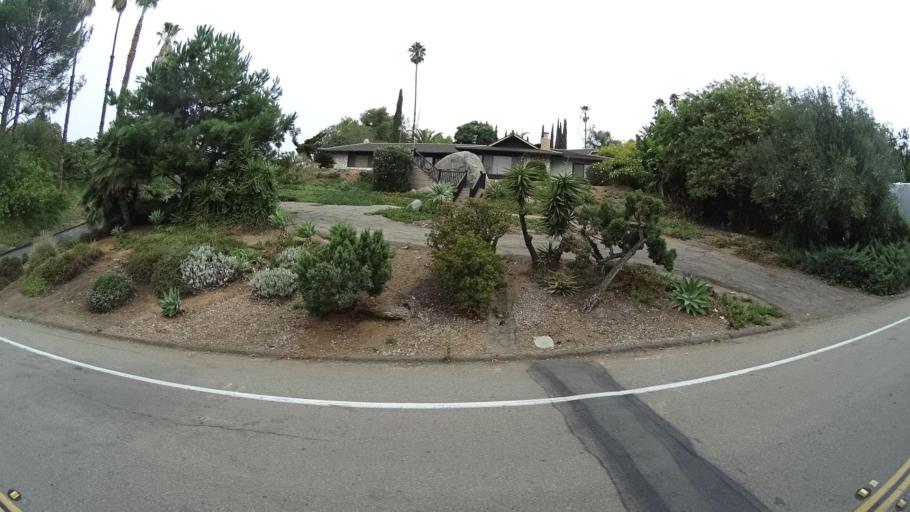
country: US
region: California
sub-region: San Diego County
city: Rancho San Diego
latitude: 32.7722
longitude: -116.9160
